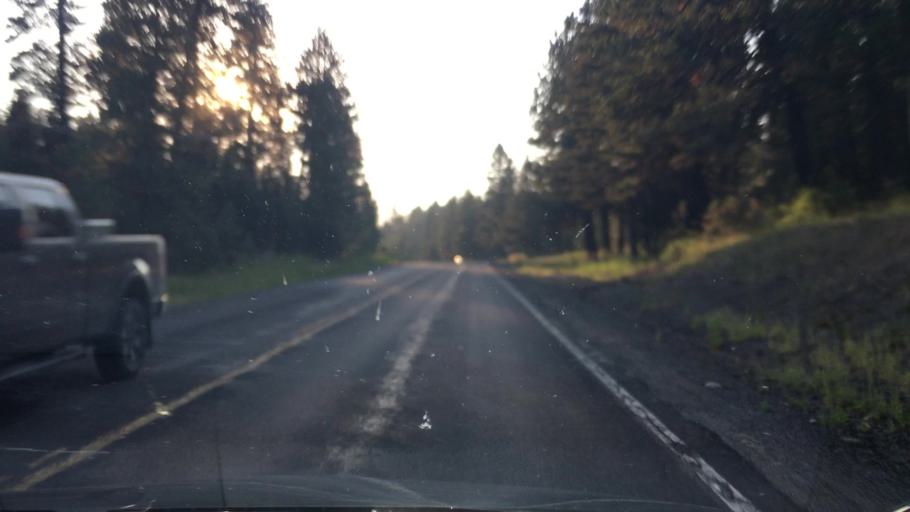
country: US
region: Idaho
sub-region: Valley County
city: McCall
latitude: 44.9281
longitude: -116.1493
